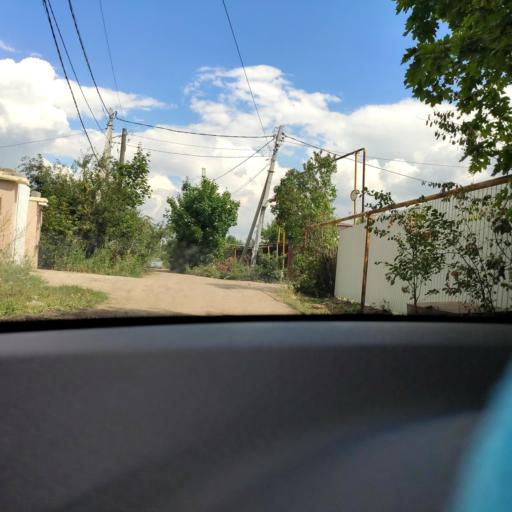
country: RU
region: Samara
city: Samara
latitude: 53.2964
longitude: 50.2301
